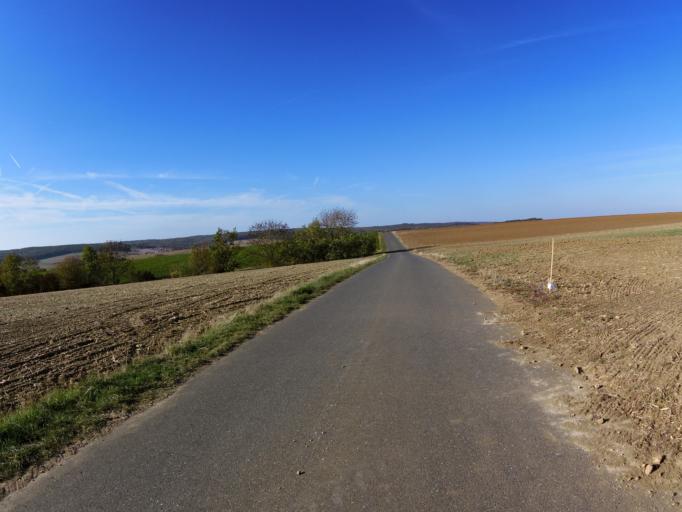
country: DE
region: Bavaria
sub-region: Regierungsbezirk Unterfranken
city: Reichenberg
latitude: 49.7152
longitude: 9.9365
